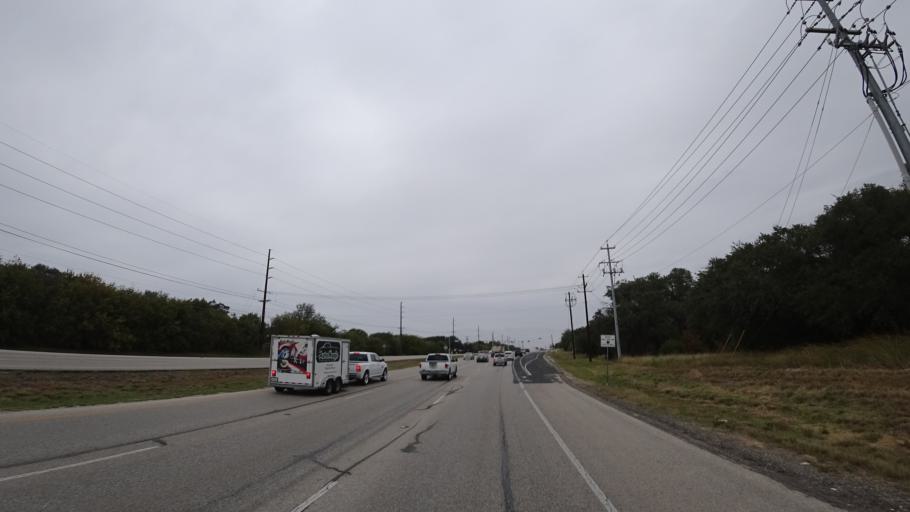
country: US
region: Texas
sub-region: Williamson County
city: Jollyville
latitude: 30.4542
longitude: -97.7518
